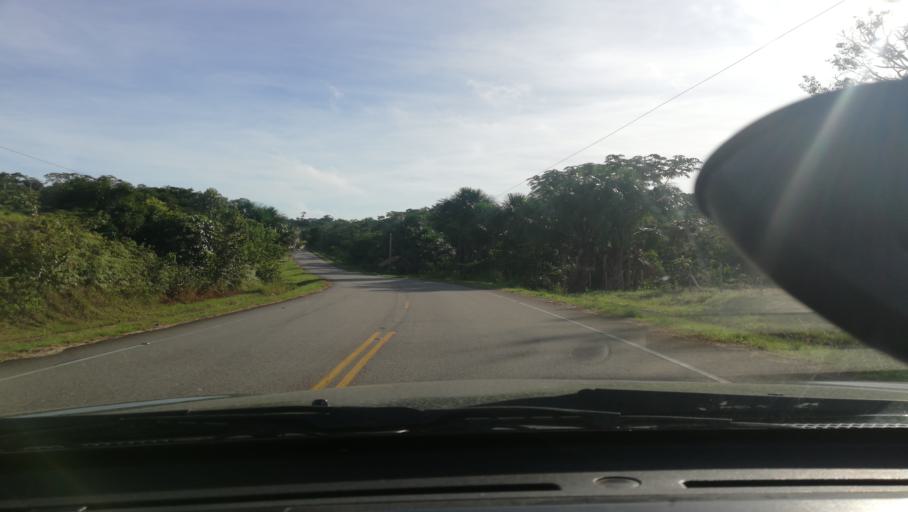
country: PE
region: Loreto
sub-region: Provincia de Loreto
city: Nauta
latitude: -4.3986
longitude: -73.5739
